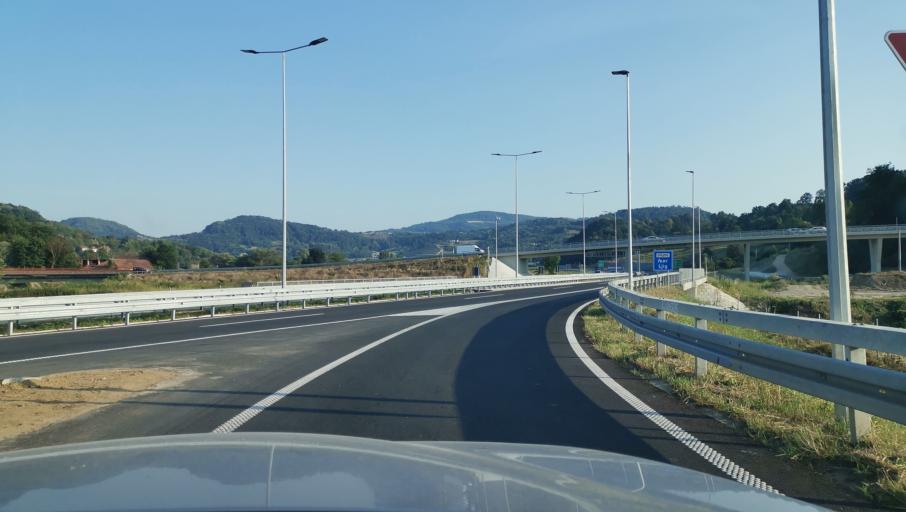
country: RS
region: Central Serbia
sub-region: Kolubarski Okrug
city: Ljig
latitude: 44.2323
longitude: 20.2538
